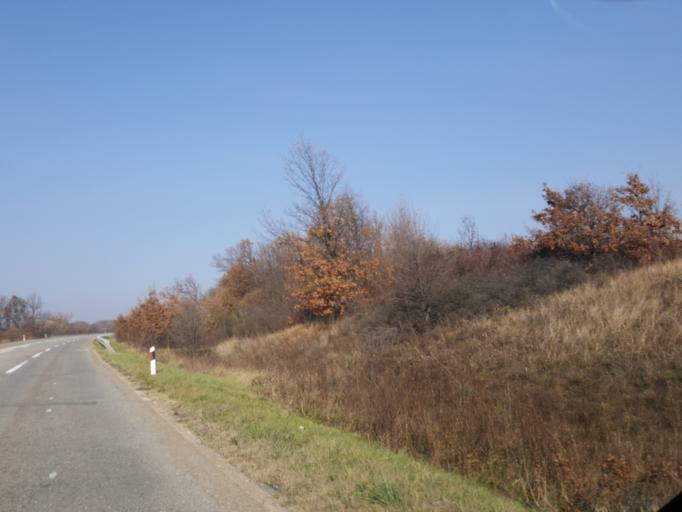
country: RS
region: Central Serbia
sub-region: Borski Okrug
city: Negotin
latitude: 44.1134
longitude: 22.3427
